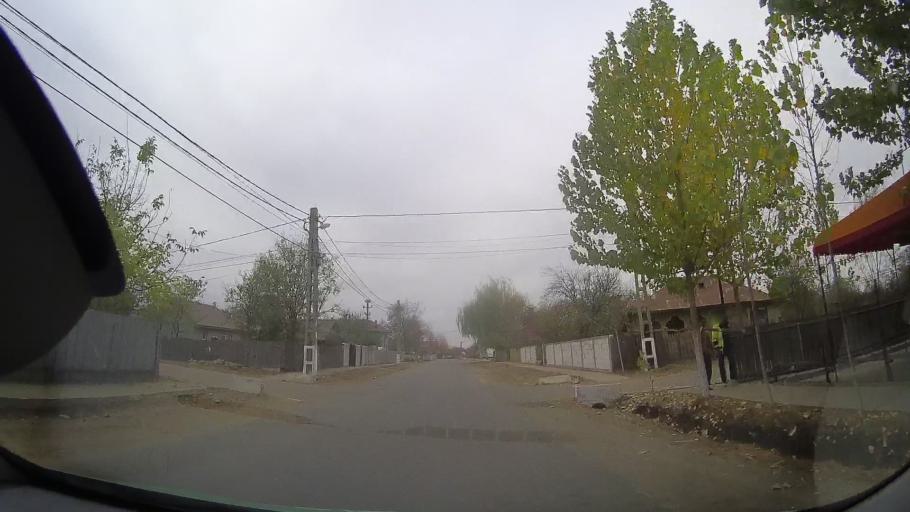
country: RO
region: Buzau
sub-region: Comuna Luciu
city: Luciu
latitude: 44.9696
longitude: 27.0848
